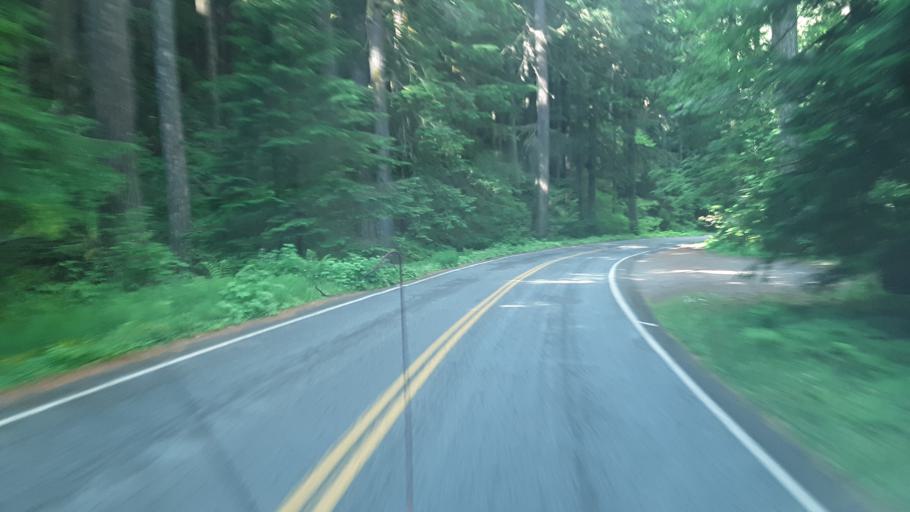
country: US
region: Washington
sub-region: Pierce County
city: Buckley
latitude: 46.7365
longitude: -121.5624
